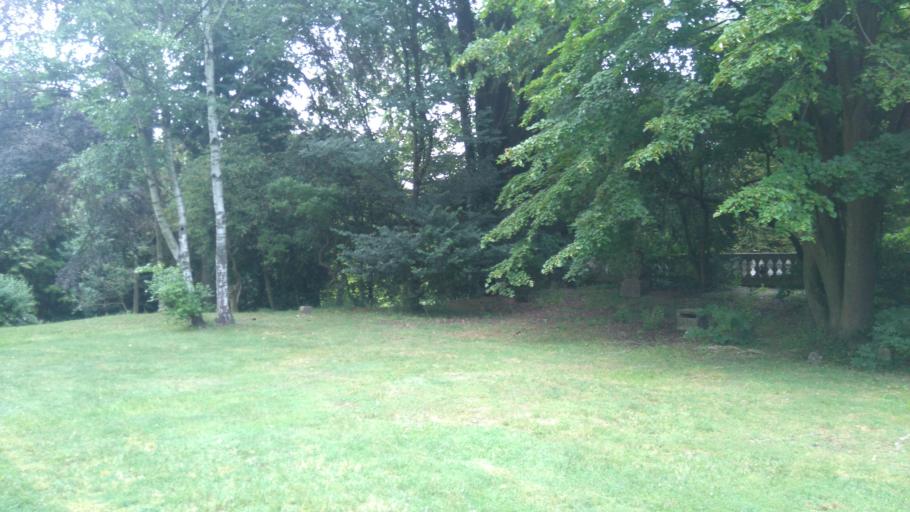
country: FR
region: Picardie
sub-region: Departement de l'Oise
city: Saint-Maximin
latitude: 49.2356
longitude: 2.4519
